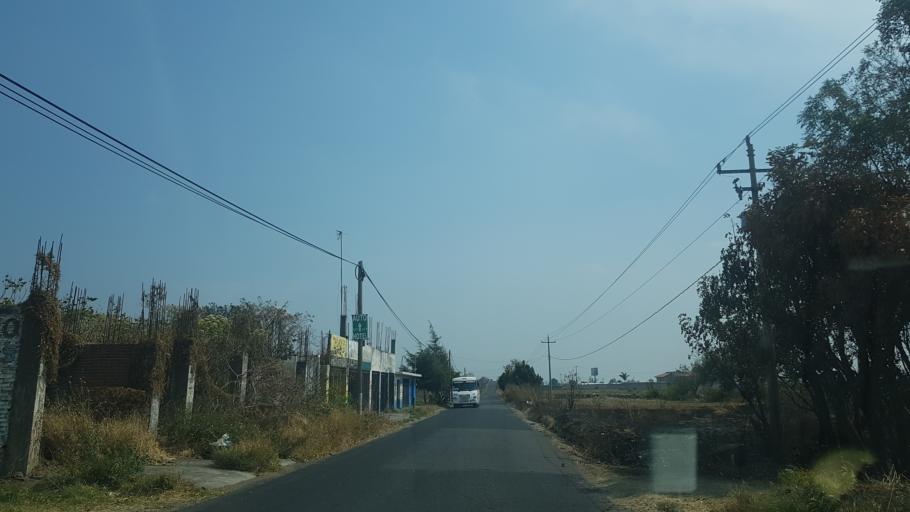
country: MX
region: Puebla
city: San Juan Tianguismanalco
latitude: 18.9405
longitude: -98.4541
